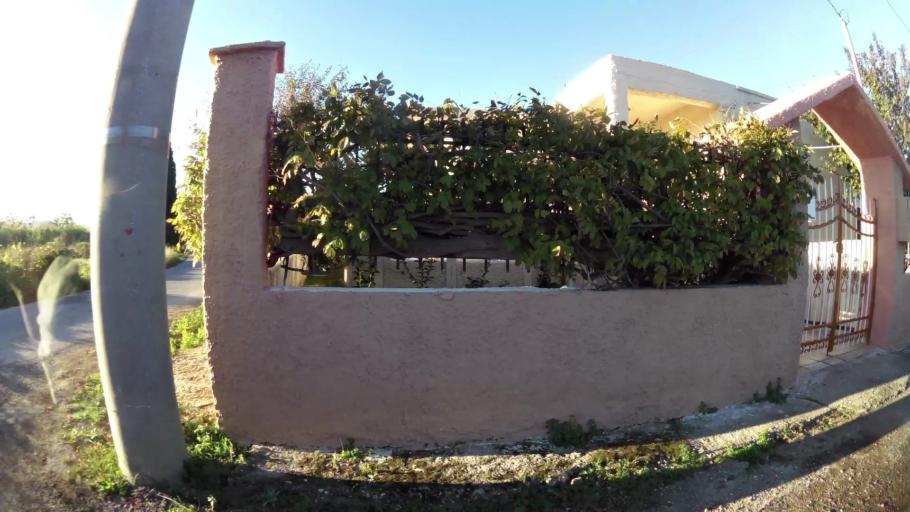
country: GR
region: Attica
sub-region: Nomarchia Anatolikis Attikis
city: Pallini
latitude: 38.0036
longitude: 23.8644
